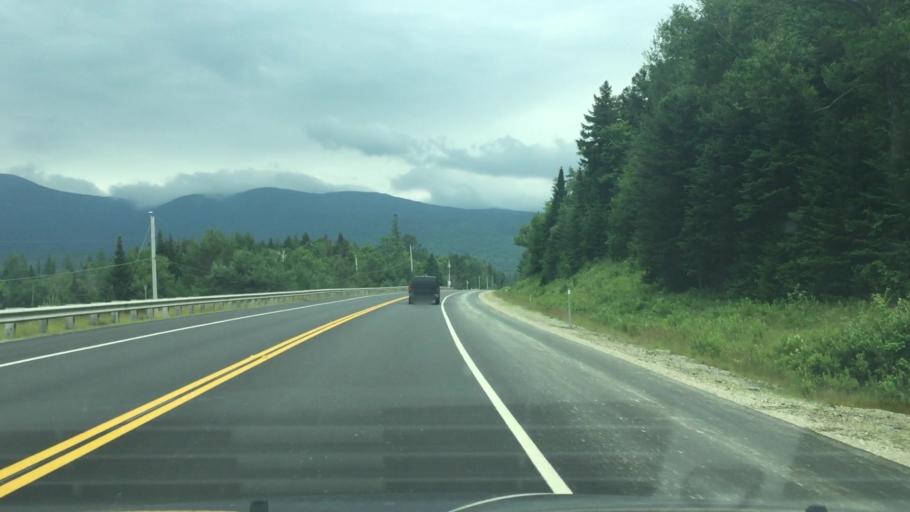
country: US
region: New Hampshire
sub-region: Coos County
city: Jefferson
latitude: 44.2521
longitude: -71.4450
